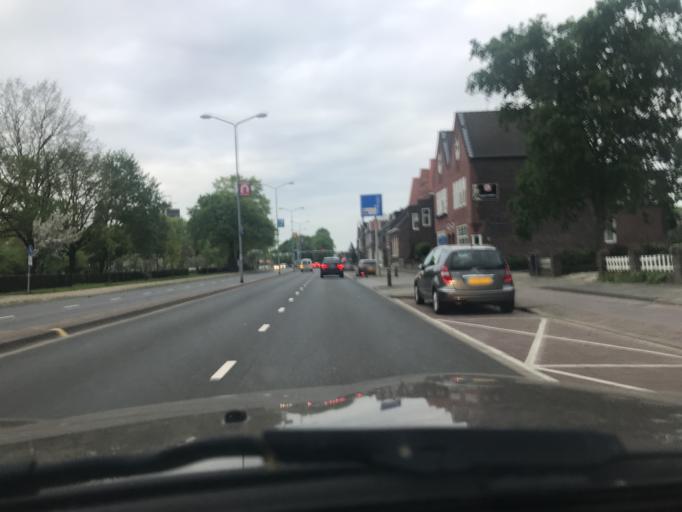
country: NL
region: Limburg
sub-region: Gemeente Venlo
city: Venlo
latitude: 51.3683
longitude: 6.1760
